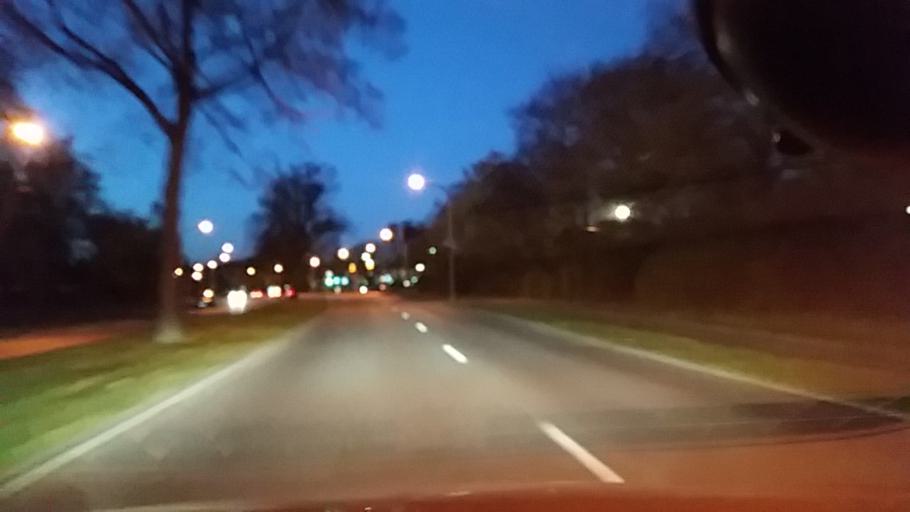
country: DE
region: Lower Saxony
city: Wolfsburg
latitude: 52.4422
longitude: 10.8072
